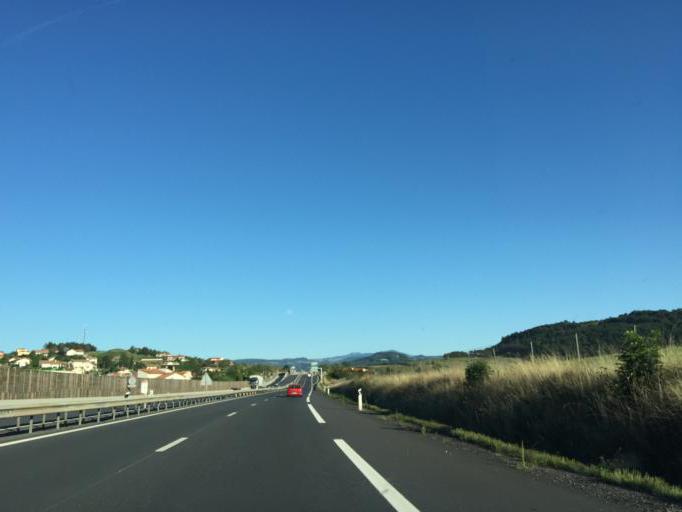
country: FR
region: Auvergne
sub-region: Departement de la Haute-Loire
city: Brives-Charensac
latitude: 45.0583
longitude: 3.9382
